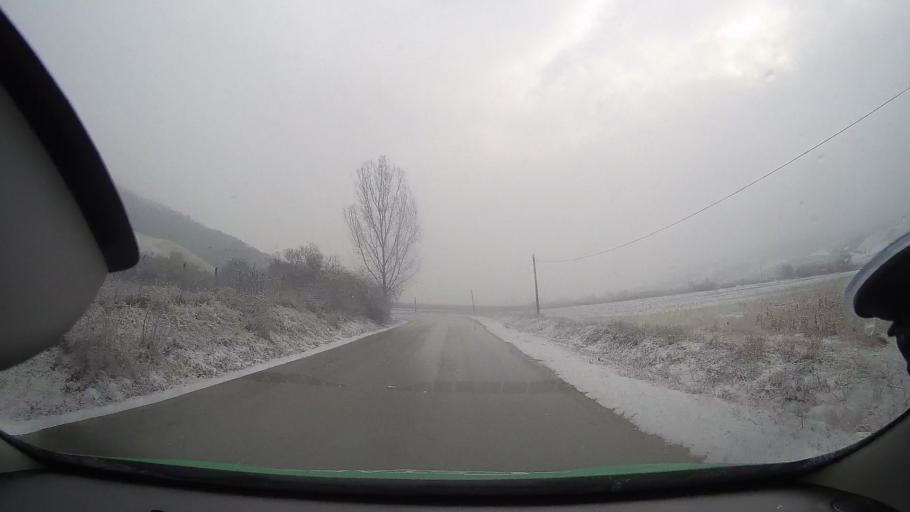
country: RO
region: Alba
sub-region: Comuna Lopadea Noua
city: Lopadea Noua
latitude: 46.3043
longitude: 23.8008
